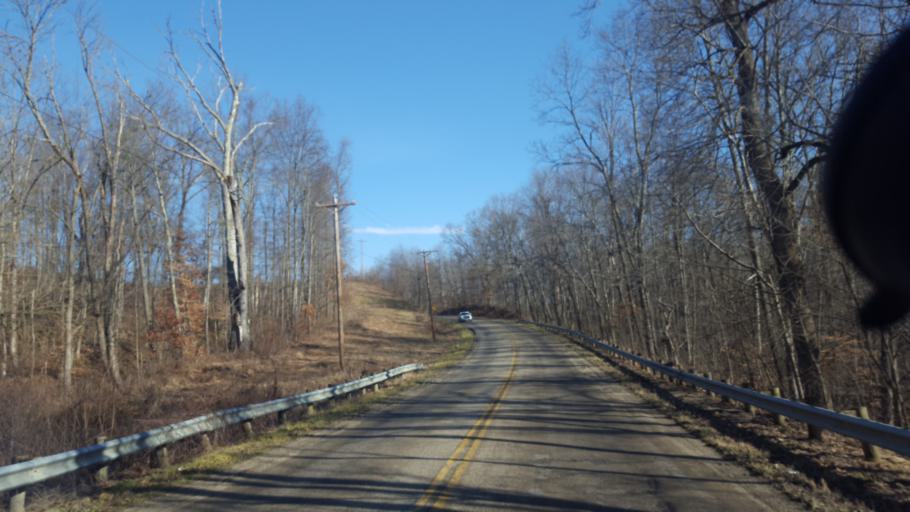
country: US
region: Ohio
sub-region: Tuscarawas County
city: Newcomerstown
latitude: 40.2270
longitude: -81.5065
